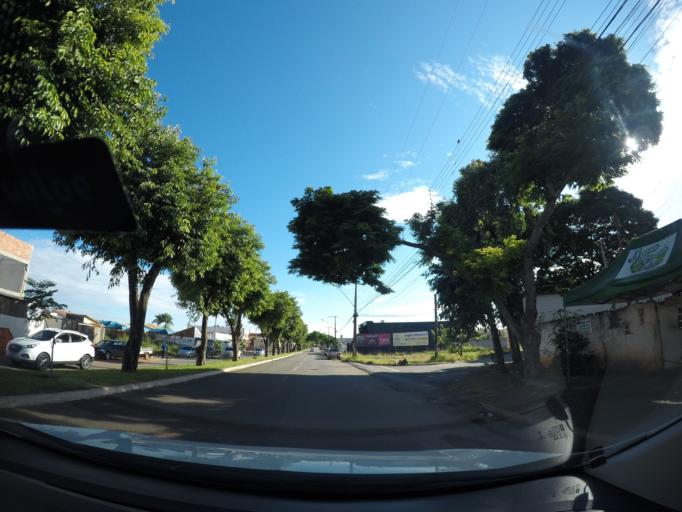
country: BR
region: Goias
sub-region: Goiania
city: Goiania
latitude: -16.7317
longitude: -49.3058
